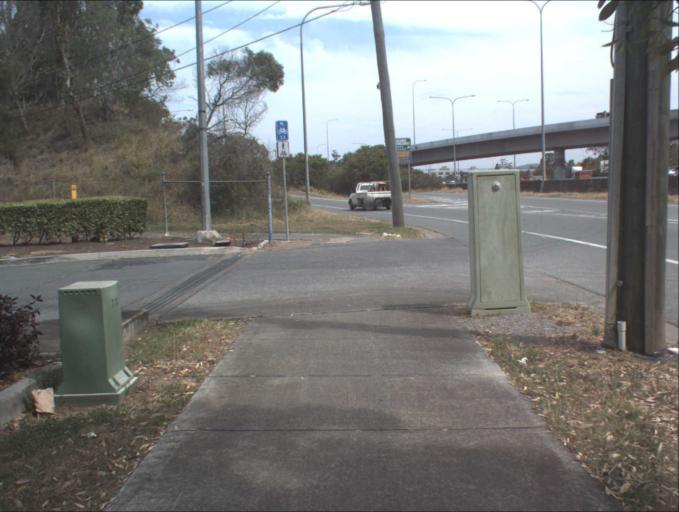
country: AU
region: Queensland
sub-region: Logan
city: Beenleigh
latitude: -27.6848
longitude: 153.1894
